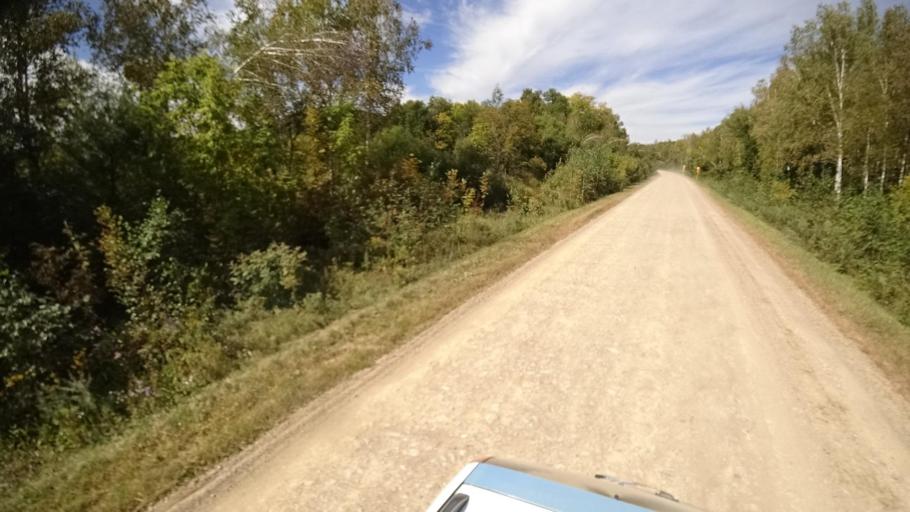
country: RU
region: Primorskiy
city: Yakovlevka
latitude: 44.6616
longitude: 133.7260
